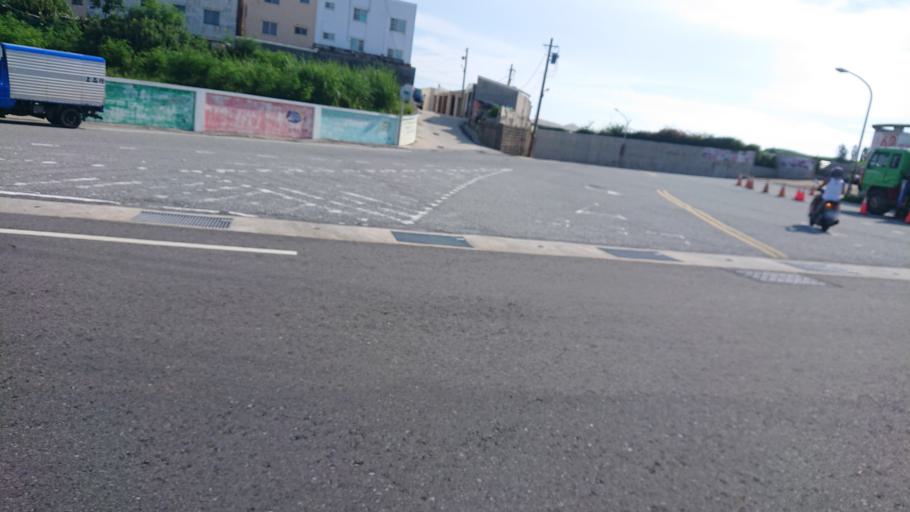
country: TW
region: Taiwan
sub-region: Penghu
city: Ma-kung
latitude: 23.5270
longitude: 119.5690
